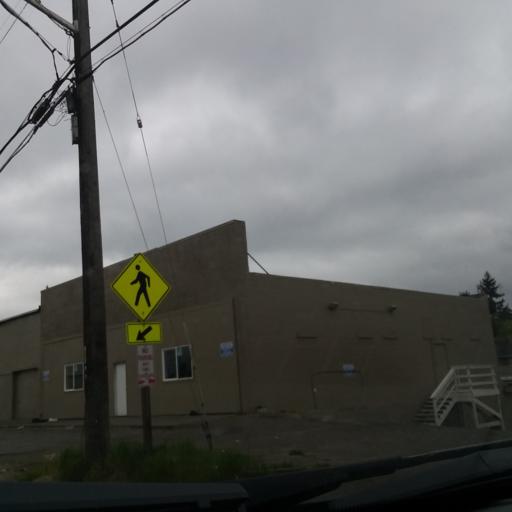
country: US
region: Washington
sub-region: King County
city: White Center
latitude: 47.5058
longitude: -122.3337
